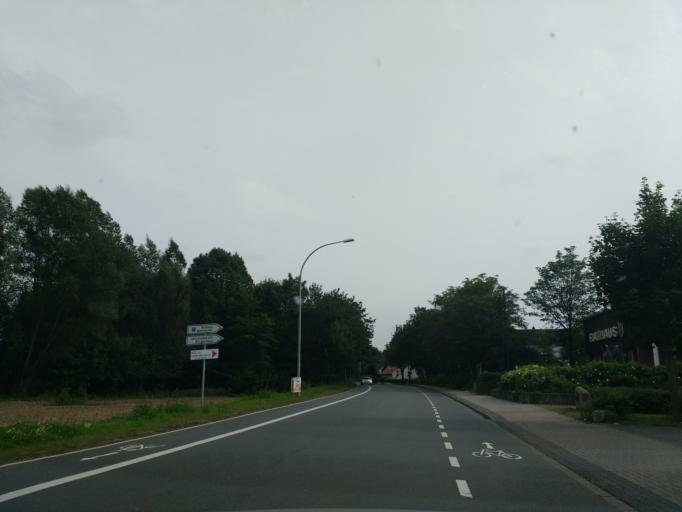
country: DE
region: North Rhine-Westphalia
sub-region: Regierungsbezirk Detmold
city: Paderborn
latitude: 51.6575
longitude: 8.7222
